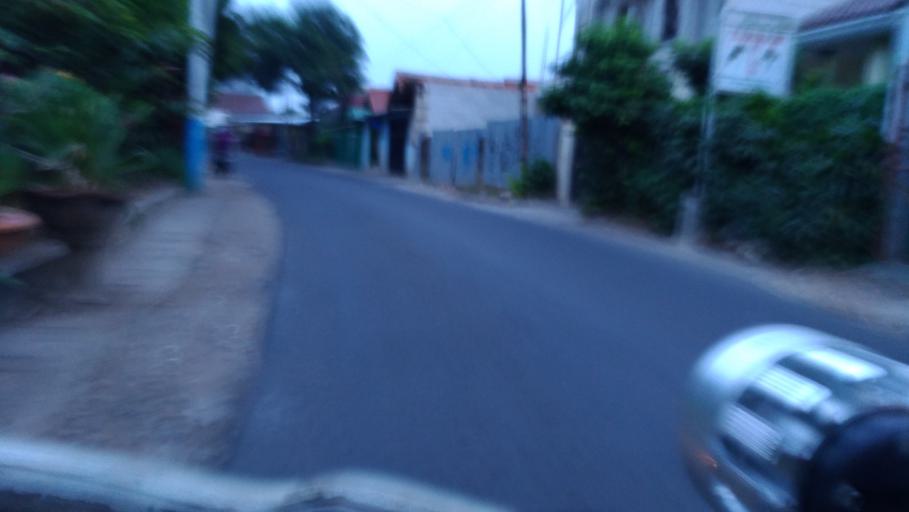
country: ID
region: West Java
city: Depok
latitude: -6.3627
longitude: 106.8842
